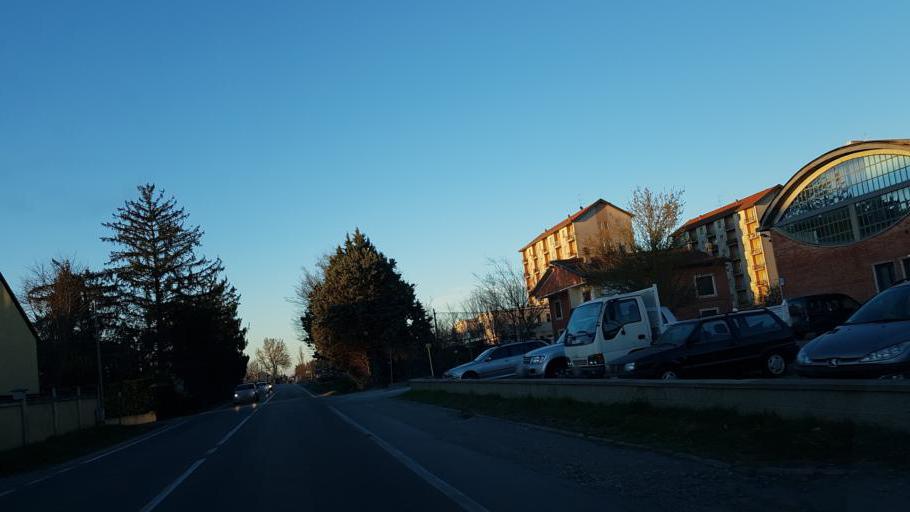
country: IT
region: Piedmont
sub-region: Provincia di Alessandria
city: Carbonara Scrivia
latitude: 44.8596
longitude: 8.8551
